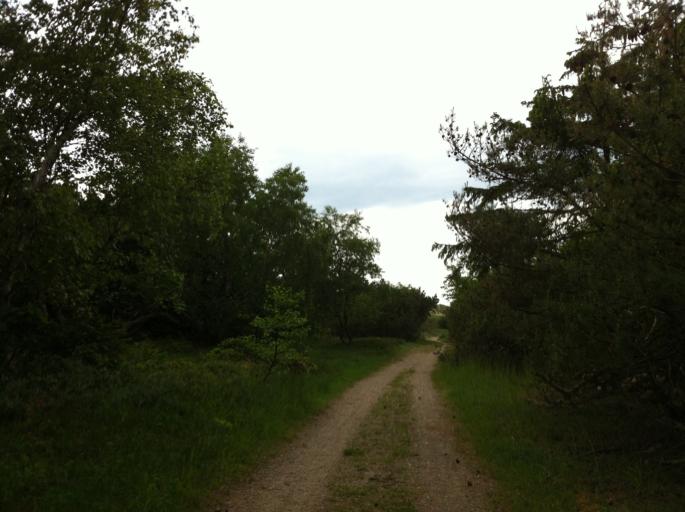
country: DK
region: Capital Region
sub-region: Halsnaes Kommune
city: Frederiksvaerk
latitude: 56.0401
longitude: 12.0335
